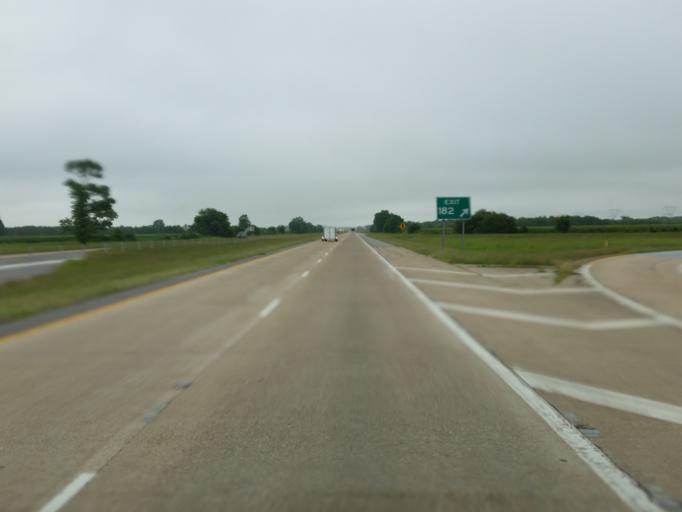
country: US
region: Mississippi
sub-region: Warren County
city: Vicksburg
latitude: 32.3296
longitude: -91.0236
